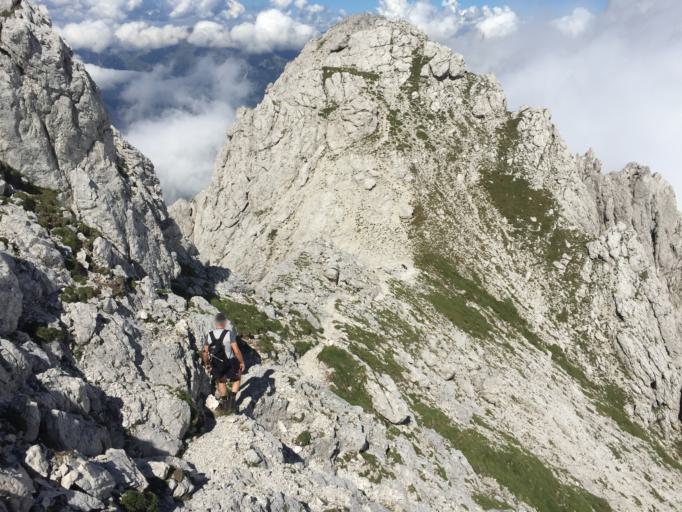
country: IT
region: Veneto
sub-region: Provincia di Belluno
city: Granvilla
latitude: 46.5427
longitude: 12.7371
